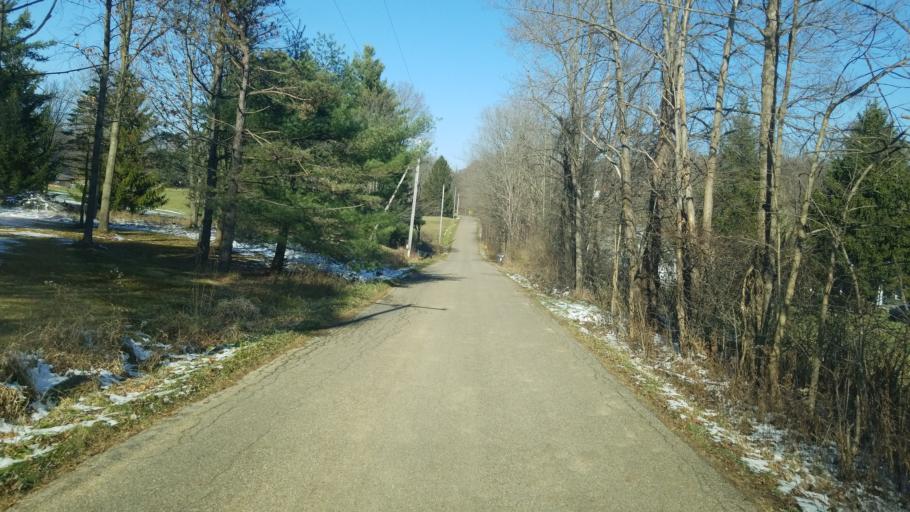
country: US
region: Ohio
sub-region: Sandusky County
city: Bellville
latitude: 40.6487
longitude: -82.4584
